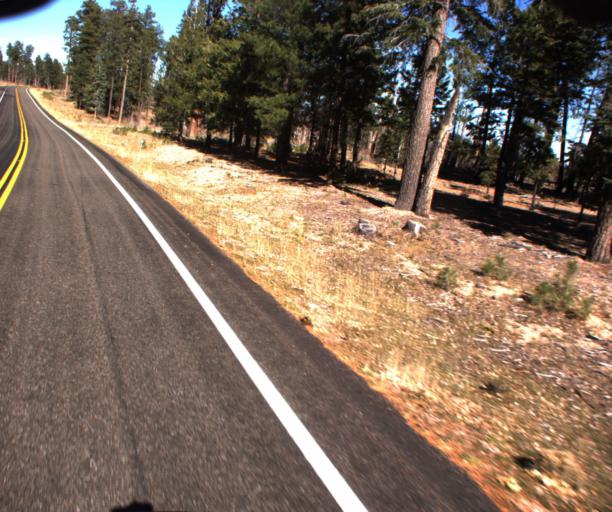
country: US
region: Arizona
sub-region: Coconino County
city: Fredonia
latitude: 36.6288
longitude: -112.1747
